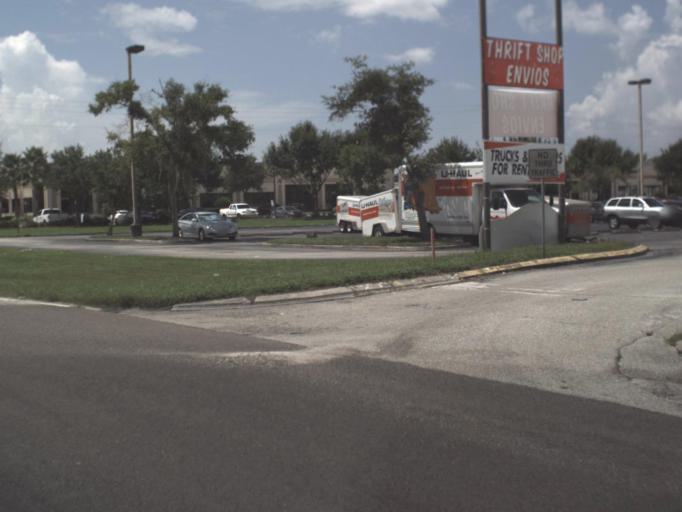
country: US
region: Florida
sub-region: Hillsborough County
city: Palm River-Clair Mel
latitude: 27.9475
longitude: -82.3541
